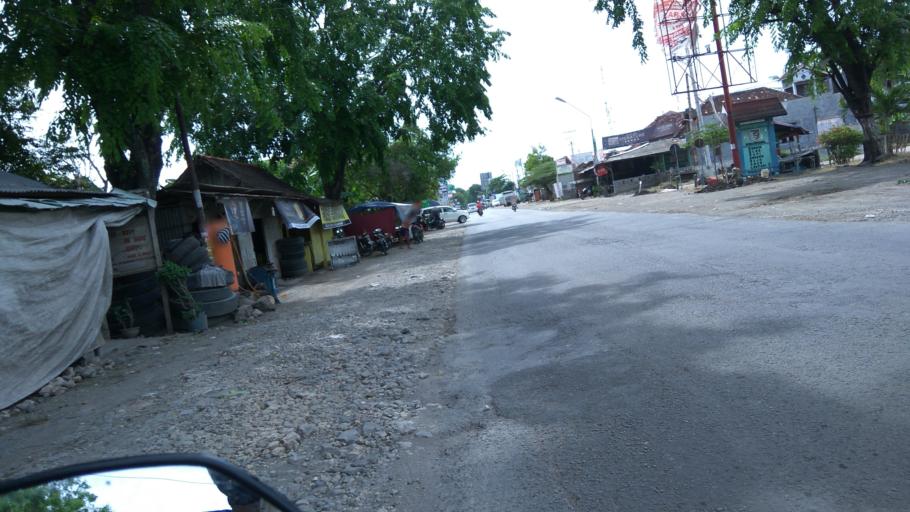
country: ID
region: Central Java
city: Mranggen
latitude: -7.0455
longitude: 110.5803
